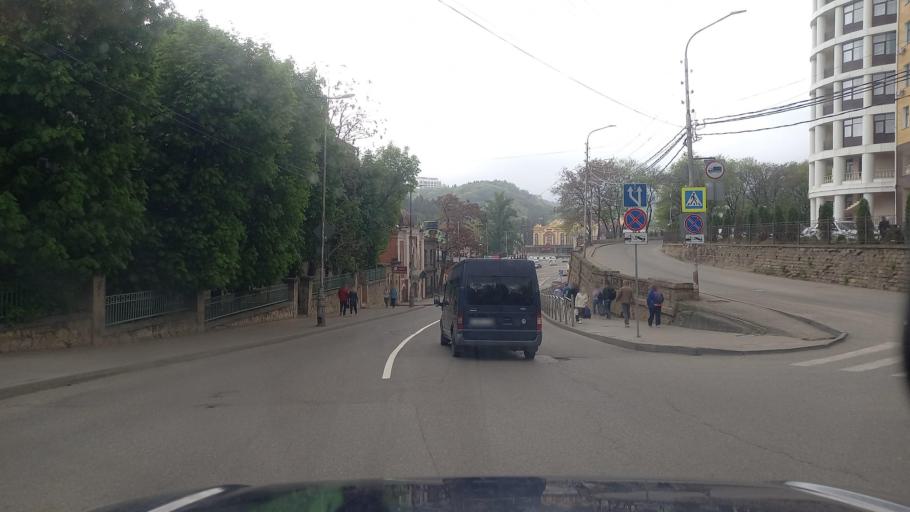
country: RU
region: Stavropol'skiy
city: Kislovodsk
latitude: 43.9076
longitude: 42.7150
